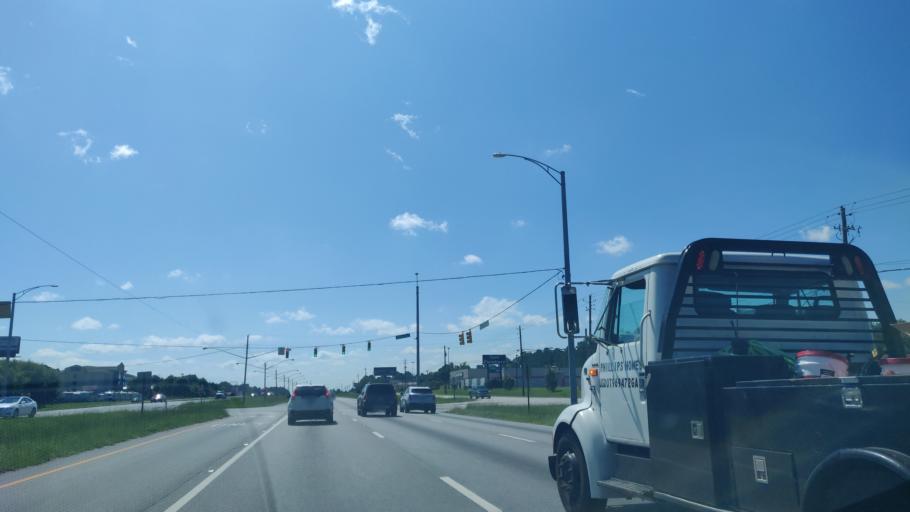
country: US
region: Alabama
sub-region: Russell County
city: Phenix City
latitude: 32.4626
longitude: -85.0223
